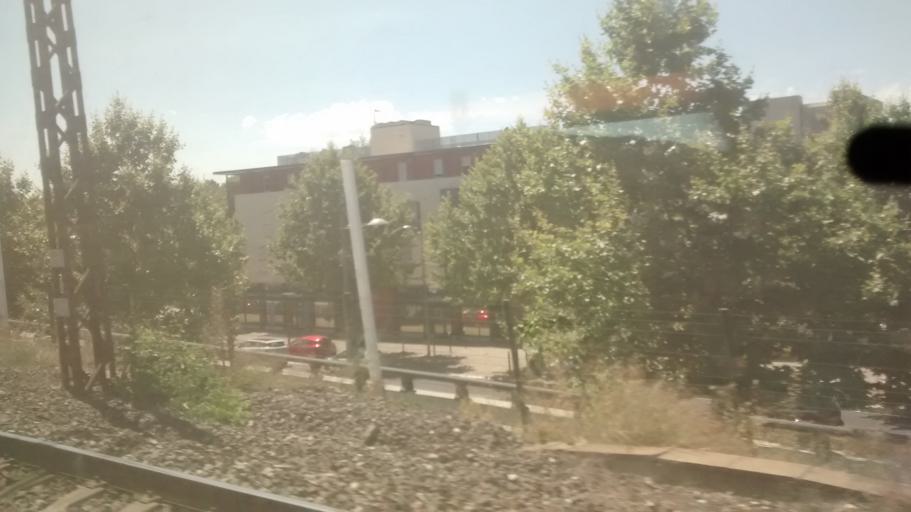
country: FR
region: Languedoc-Roussillon
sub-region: Departement de l'Herault
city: Montpellier
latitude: 43.6154
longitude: 3.8845
